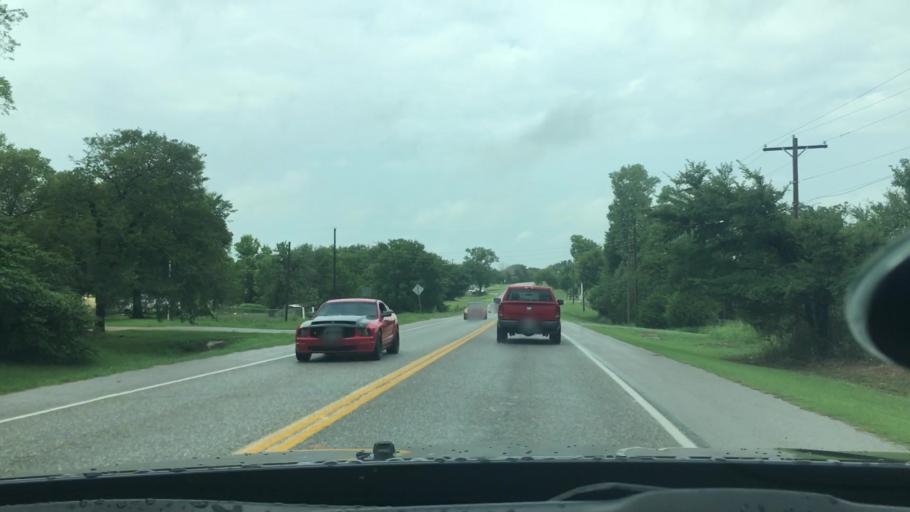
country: US
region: Oklahoma
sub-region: Johnston County
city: Tishomingo
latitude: 34.2449
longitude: -96.7532
